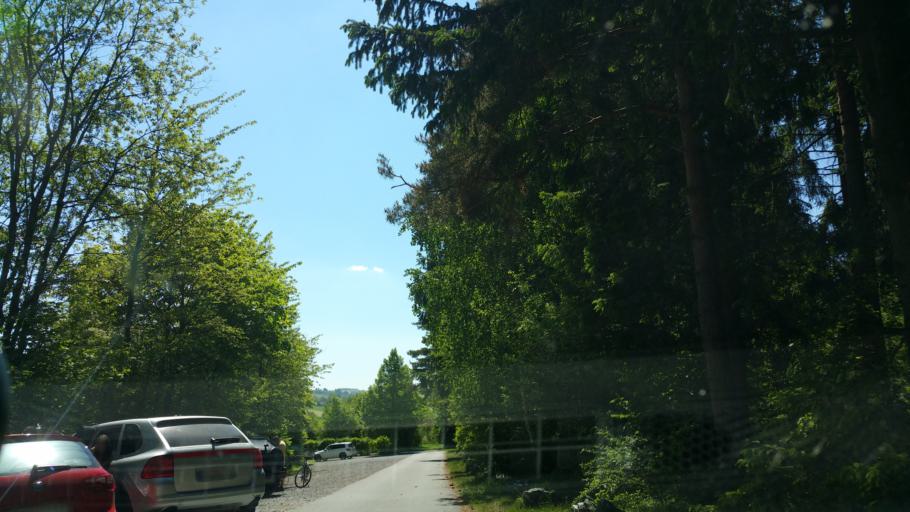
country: DE
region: Bavaria
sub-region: Upper Franconia
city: Schwarzenbach an der Saale
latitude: 50.2024
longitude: 11.9117
